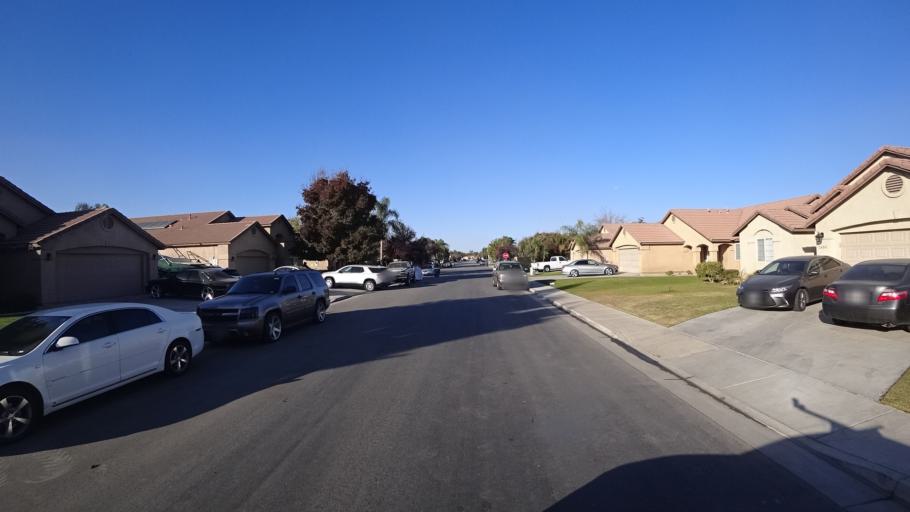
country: US
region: California
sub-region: Kern County
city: Greenfield
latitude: 35.2770
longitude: -119.0293
